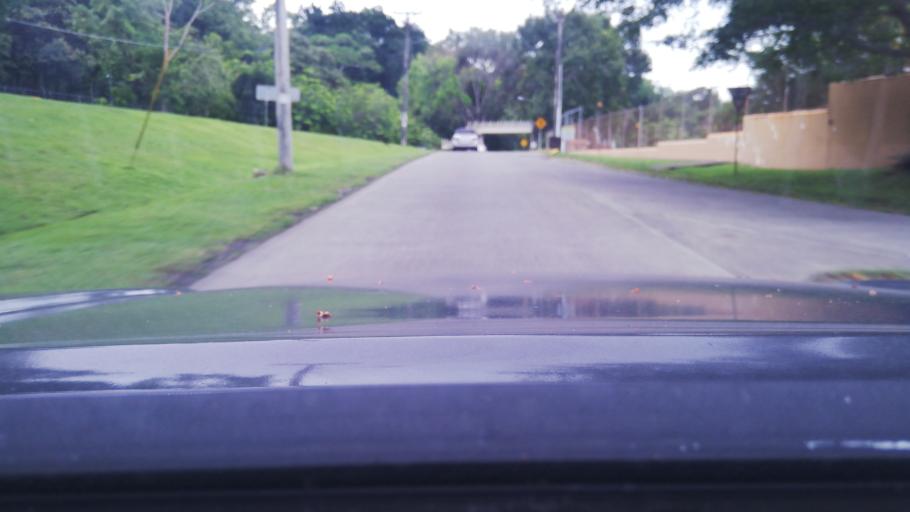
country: PA
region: Panama
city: Panama
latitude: 9.0036
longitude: -79.5452
